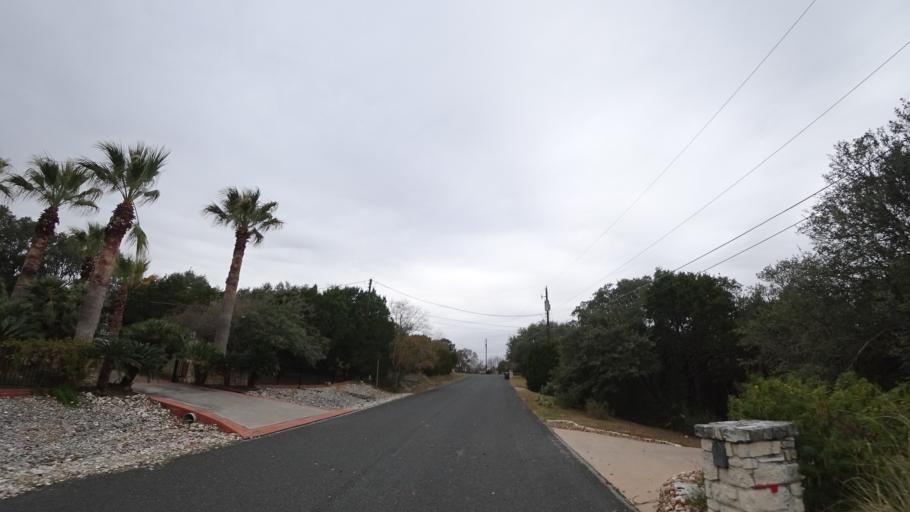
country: US
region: Texas
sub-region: Williamson County
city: Jollyville
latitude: 30.3790
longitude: -97.8135
